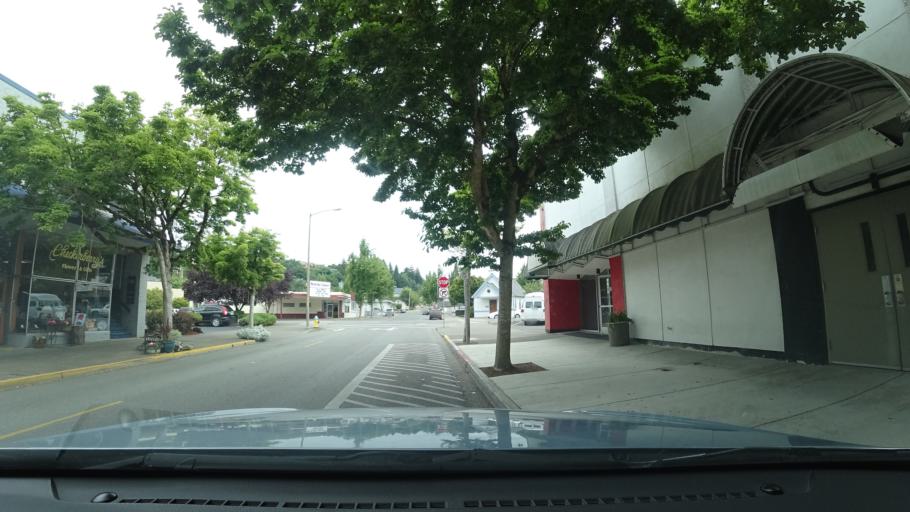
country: US
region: Oregon
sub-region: Coos County
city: Coos Bay
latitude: 43.3683
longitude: -124.2140
